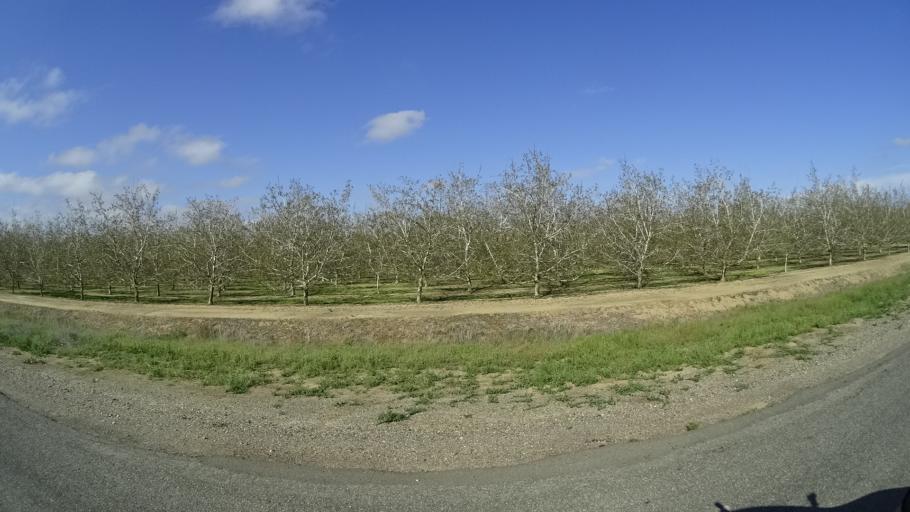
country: US
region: California
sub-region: Butte County
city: Durham
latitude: 39.4971
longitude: -121.9677
